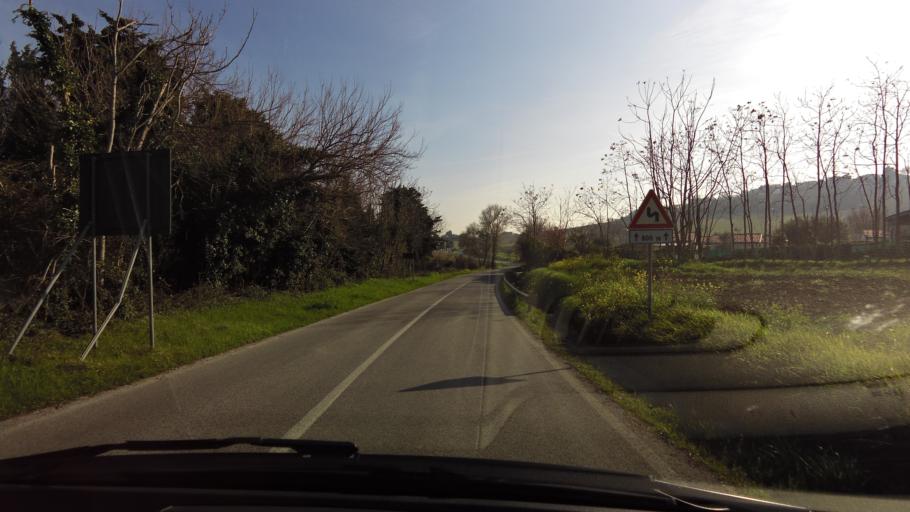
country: IT
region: The Marches
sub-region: Provincia di Ancona
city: Marcelli
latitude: 43.4989
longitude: 13.6167
